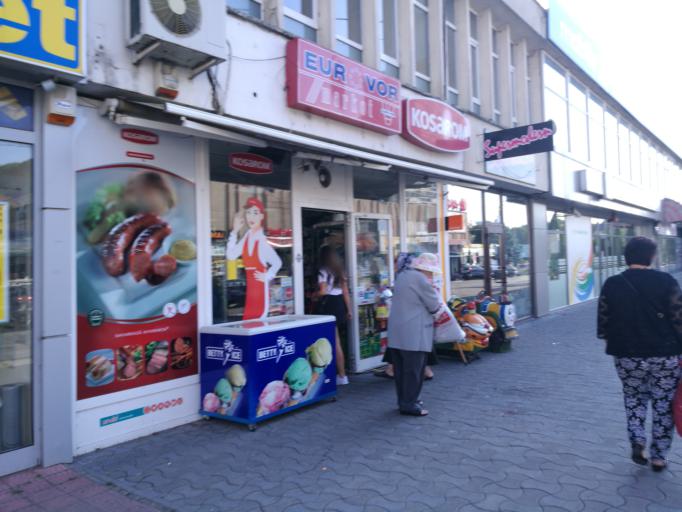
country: RO
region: Neamt
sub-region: Municipiul Piatra-Neamt
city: Valeni
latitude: 46.9314
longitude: 26.3723
